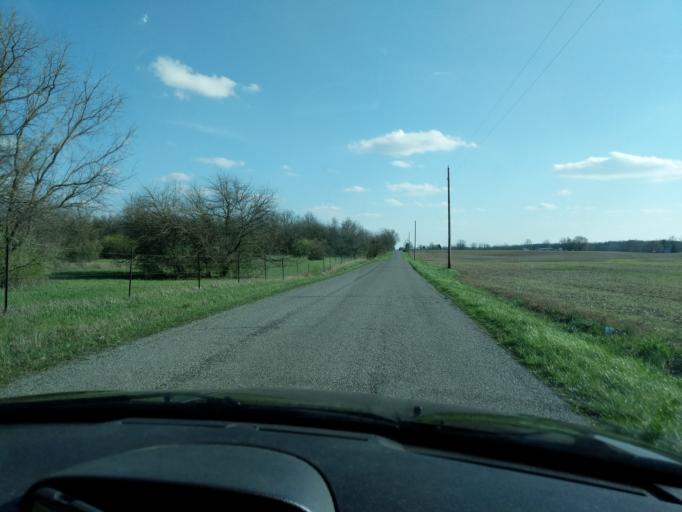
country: US
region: Ohio
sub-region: Champaign County
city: Urbana
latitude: 40.1618
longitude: -83.8326
